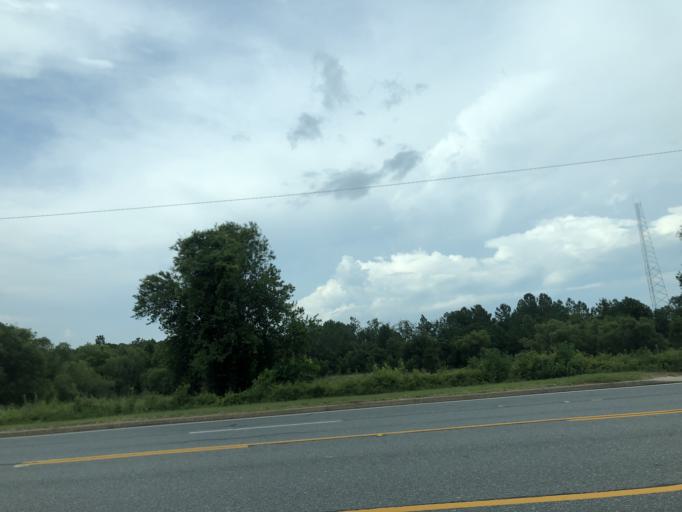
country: US
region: Georgia
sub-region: Wayne County
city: Jesup
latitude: 31.6196
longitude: -81.8996
